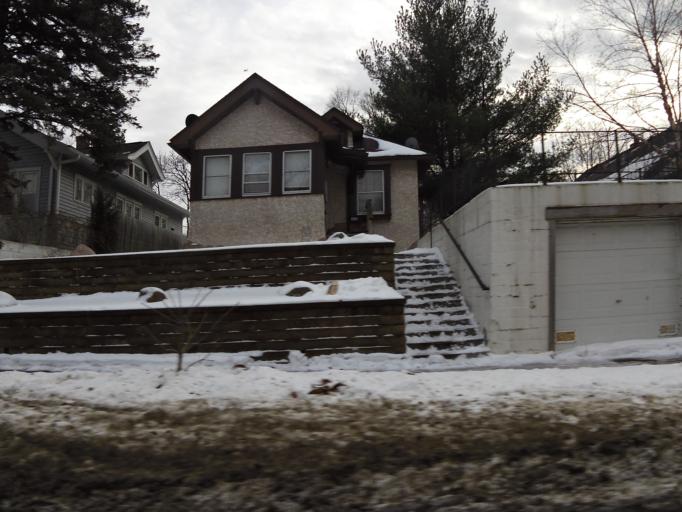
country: US
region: Minnesota
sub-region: Ramsey County
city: Maplewood
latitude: 44.9667
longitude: -93.0323
